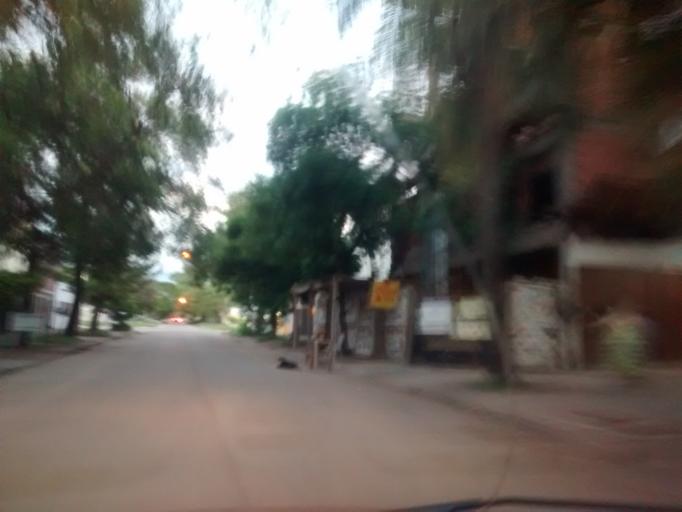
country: AR
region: Chaco
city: Resistencia
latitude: -27.4477
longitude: -58.9775
